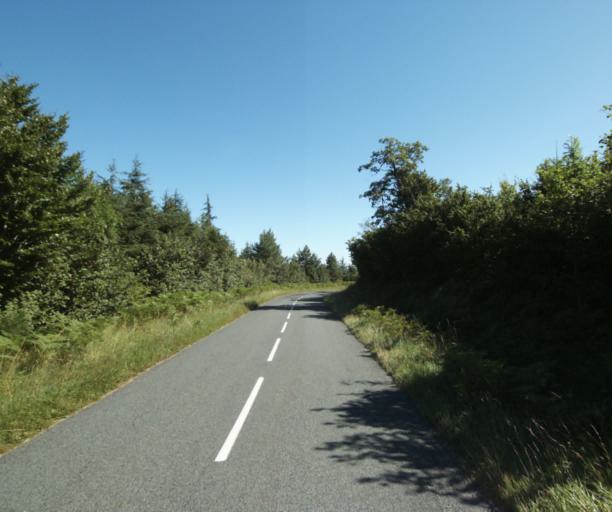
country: FR
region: Midi-Pyrenees
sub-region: Departement du Tarn
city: Dourgne
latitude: 43.4413
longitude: 2.1427
